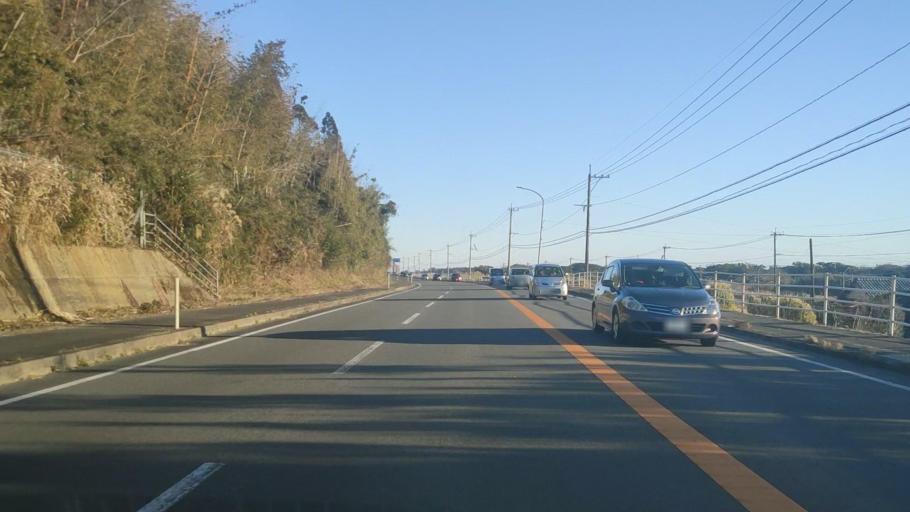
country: JP
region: Miyazaki
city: Takanabe
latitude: 32.1086
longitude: 131.5253
